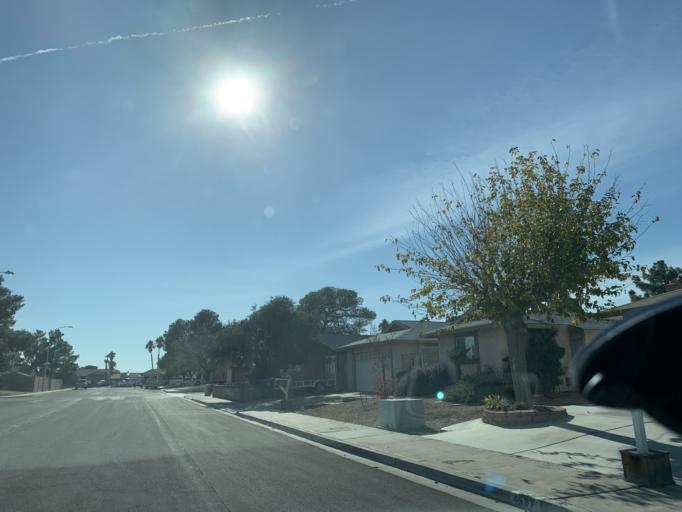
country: US
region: Nevada
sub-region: Clark County
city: Spring Valley
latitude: 36.1065
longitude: -115.2334
